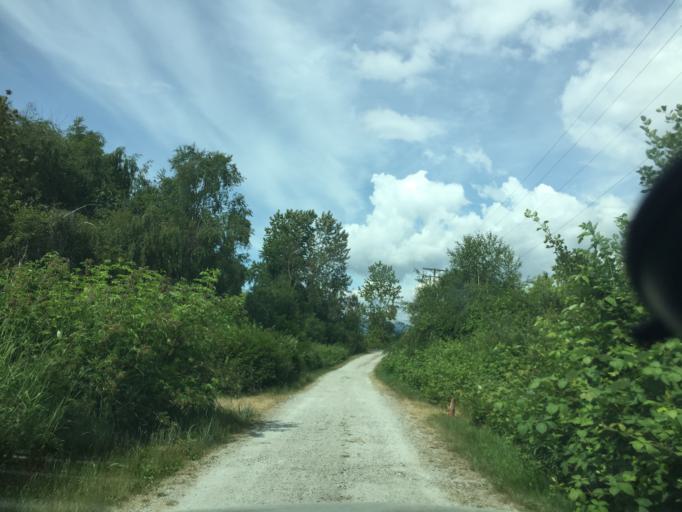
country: CA
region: British Columbia
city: Richmond
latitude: 49.2097
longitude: -123.1922
